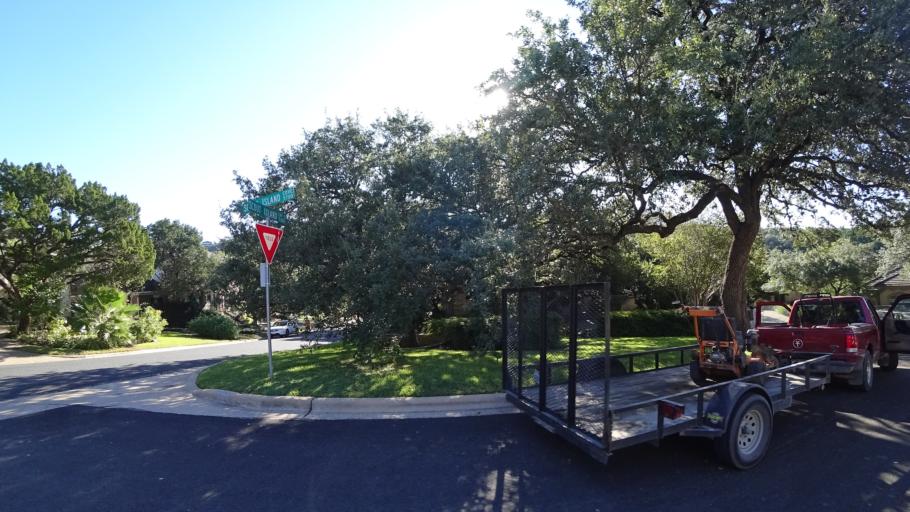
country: US
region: Texas
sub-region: Travis County
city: West Lake Hills
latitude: 30.3536
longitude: -97.7877
